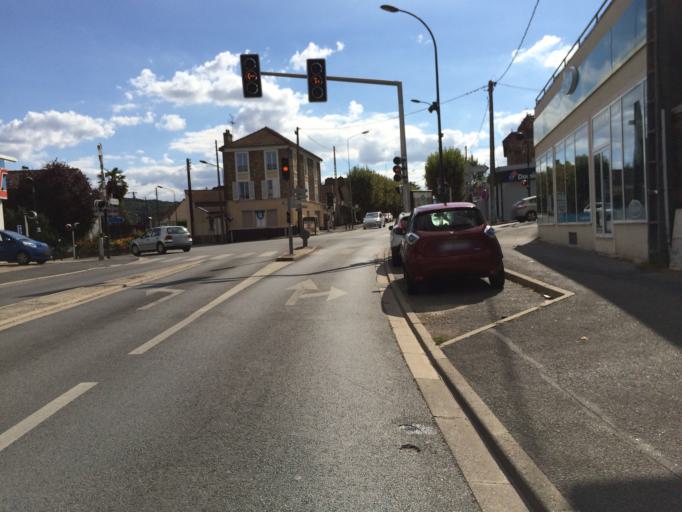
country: FR
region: Ile-de-France
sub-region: Departement de l'Essonne
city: Villebon-sur-Yvette
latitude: 48.7071
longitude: 2.2394
